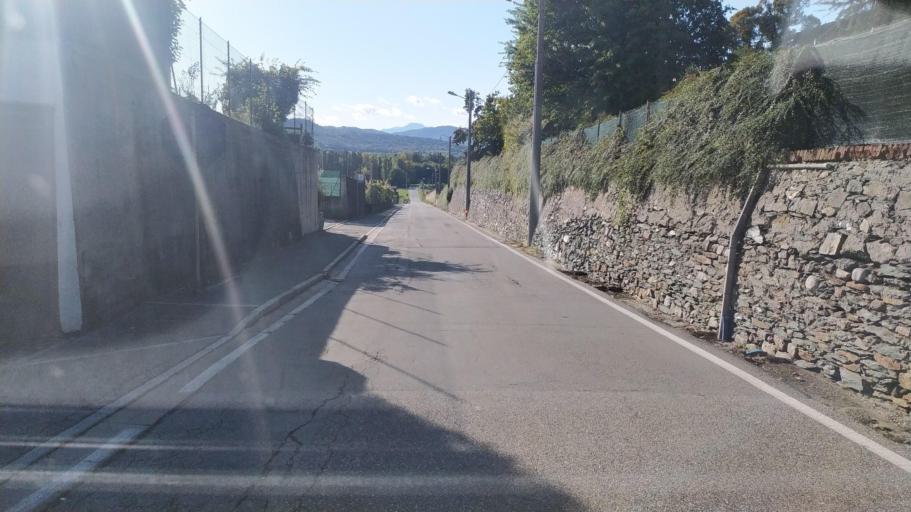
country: IT
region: Lombardy
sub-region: Provincia di Varese
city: Ispra
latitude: 45.7980
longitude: 8.6212
